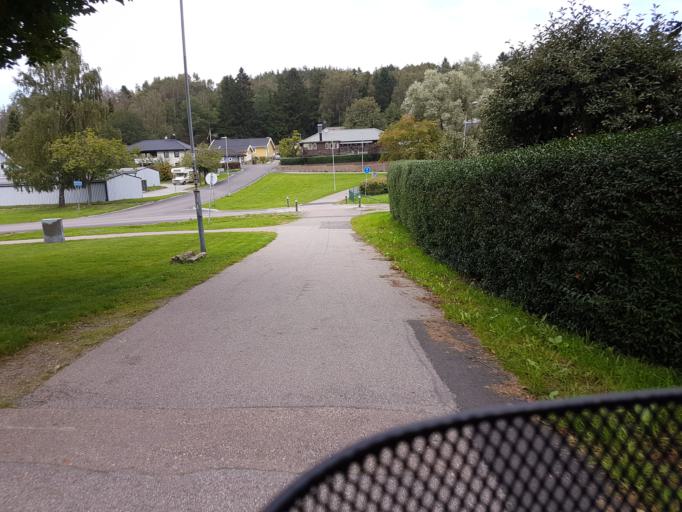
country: SE
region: Vaestra Goetaland
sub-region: Ale Kommun
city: Nodinge-Nol
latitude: 57.9077
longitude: 12.0618
